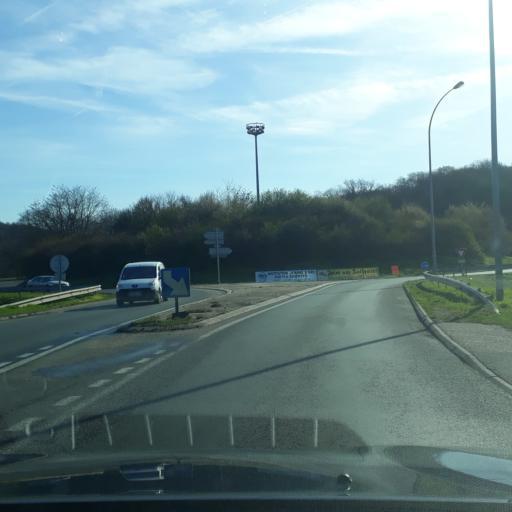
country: FR
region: Ile-de-France
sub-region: Departement de l'Essonne
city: Morigny-Champigny
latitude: 48.4338
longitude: 2.1849
